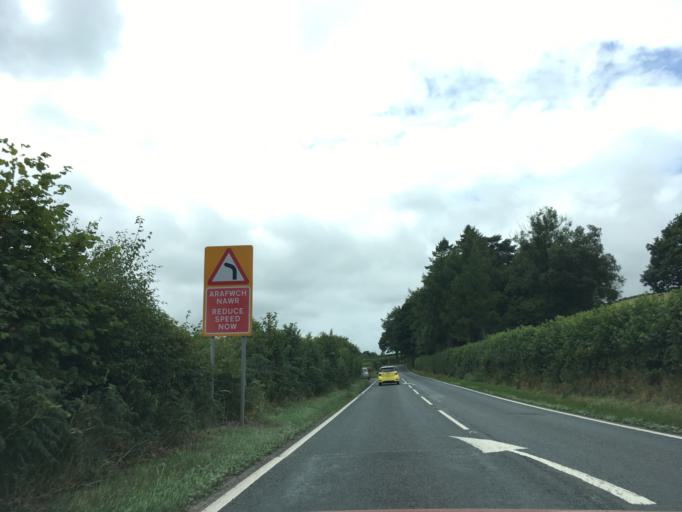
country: GB
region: Wales
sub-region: Sir Powys
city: Cray
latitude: 51.9522
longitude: -3.6119
